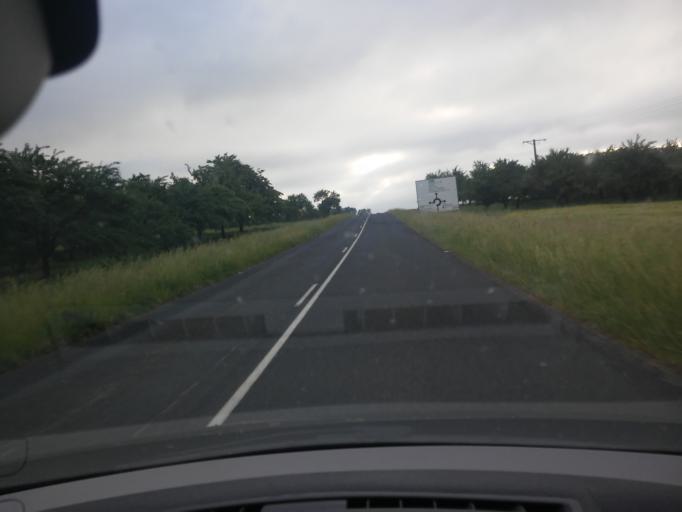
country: FR
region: Lorraine
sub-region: Departement de la Meuse
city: Vigneulles-les-Hattonchatel
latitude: 48.9739
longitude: 5.6968
